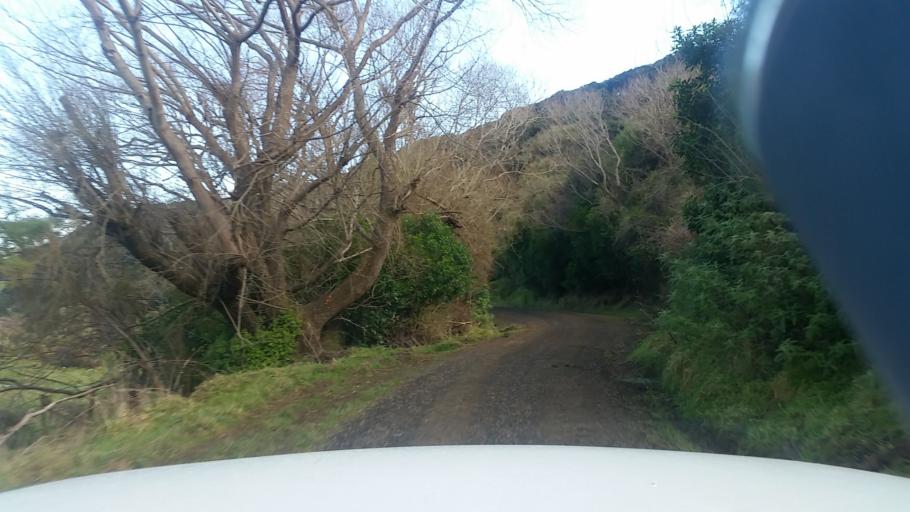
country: NZ
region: Canterbury
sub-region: Christchurch City
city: Christchurch
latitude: -43.7585
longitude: 172.9774
